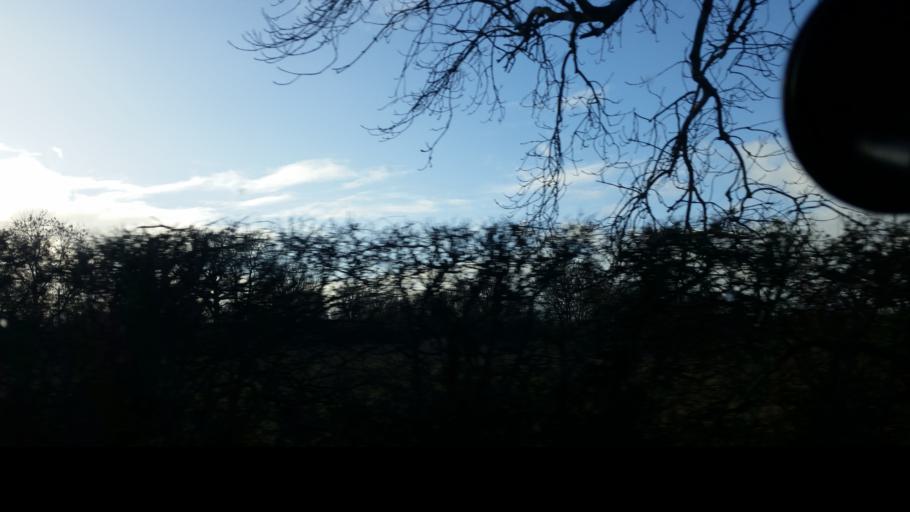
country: IE
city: Kentstown
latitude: 53.6049
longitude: -6.4733
